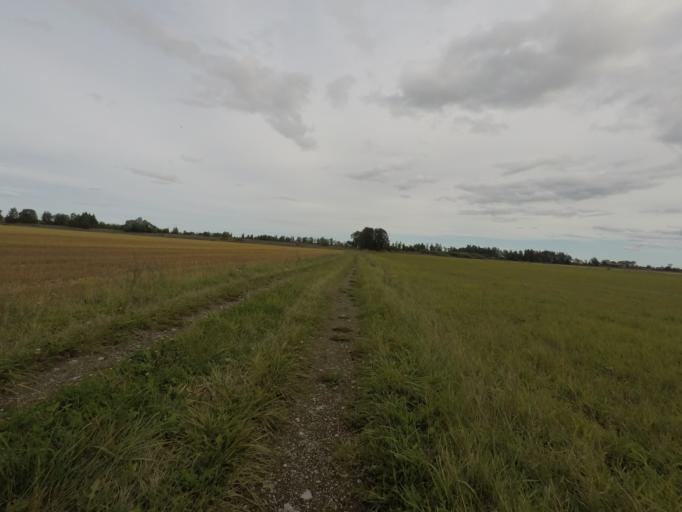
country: SE
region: Vaestmanland
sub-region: Kungsors Kommun
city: Kungsoer
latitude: 59.4593
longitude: 16.0570
